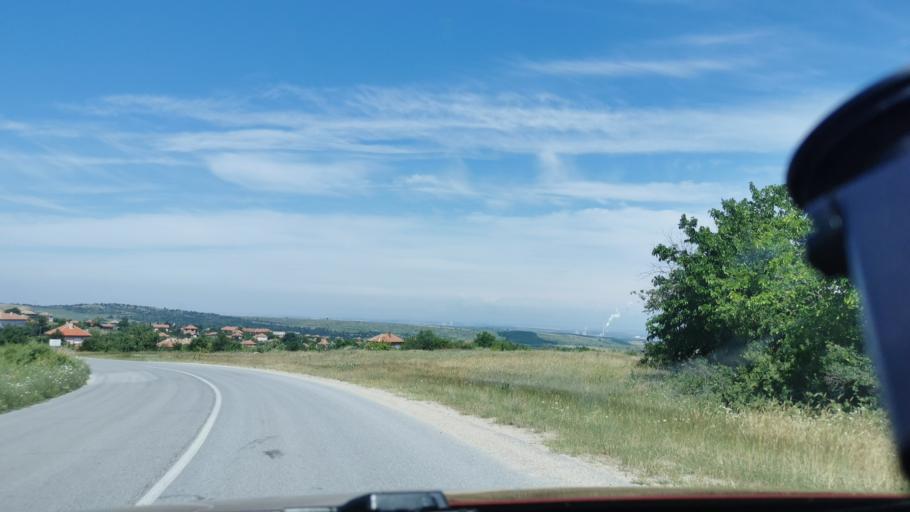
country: BG
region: Khaskovo
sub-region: Obshtina Topolovgrad
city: Topolovgrad
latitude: 42.0649
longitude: 26.1160
